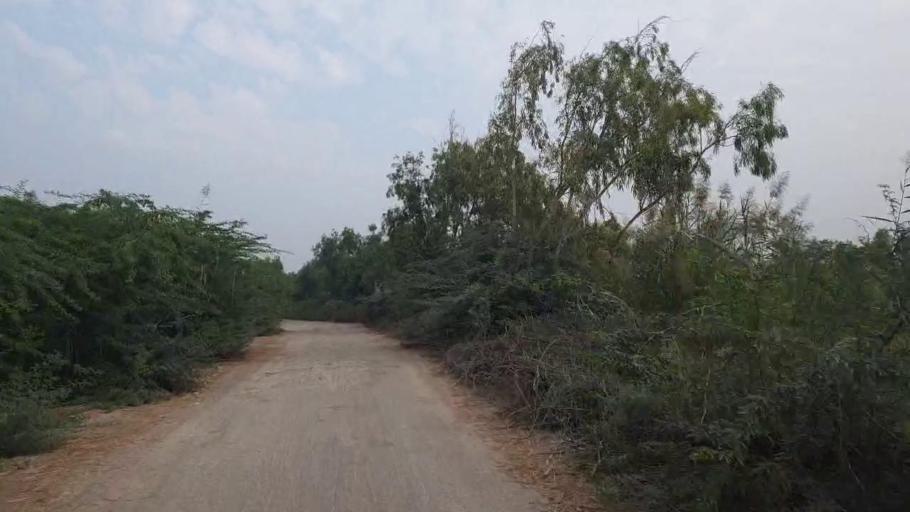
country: PK
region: Sindh
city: Talhar
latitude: 24.8330
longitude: 68.8806
